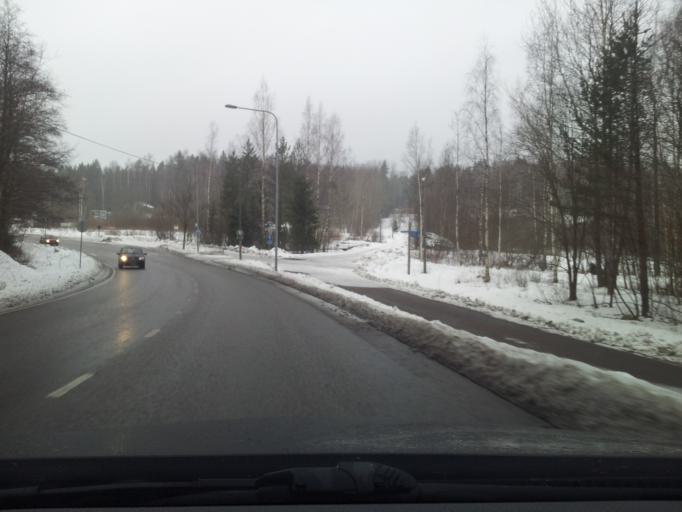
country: FI
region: Uusimaa
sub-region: Helsinki
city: Kauniainen
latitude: 60.1762
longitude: 24.7184
